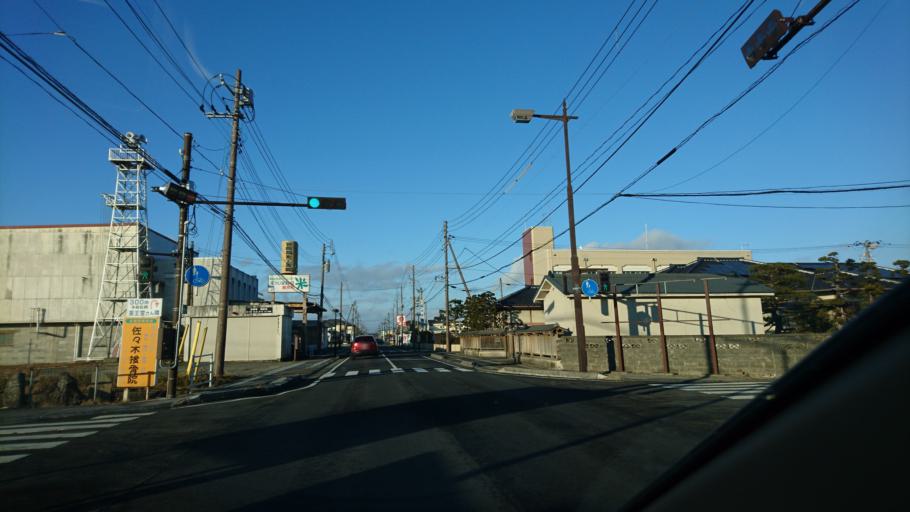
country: JP
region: Miyagi
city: Furukawa
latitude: 38.5652
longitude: 140.8594
